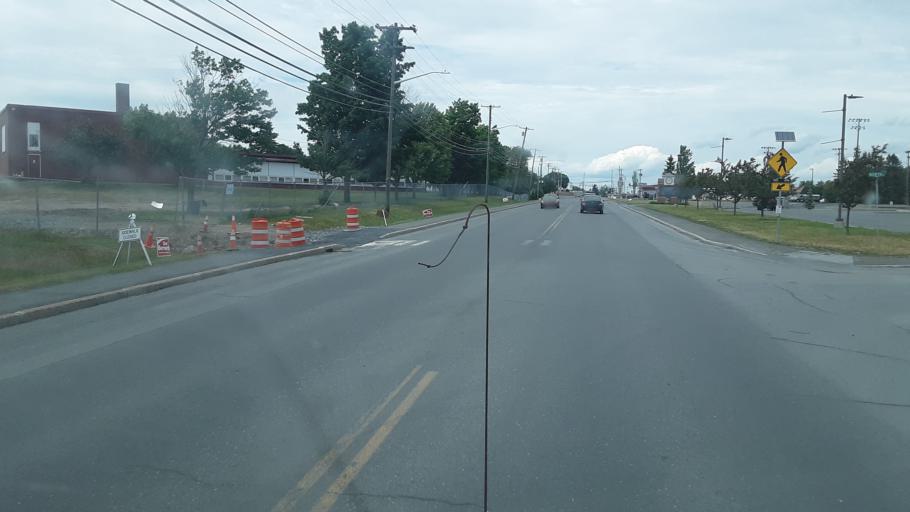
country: US
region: Maine
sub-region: Aroostook County
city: Caribou
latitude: 46.8639
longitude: -68.0049
